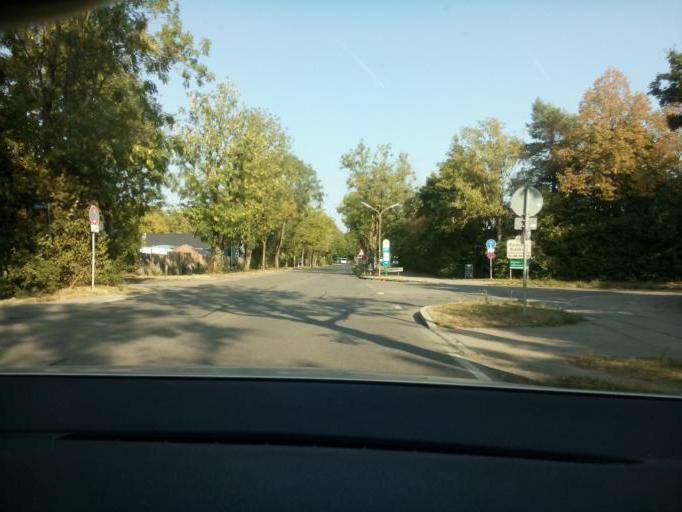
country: DE
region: Bavaria
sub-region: Upper Bavaria
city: Neubiberg
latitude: 48.0820
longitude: 11.6463
